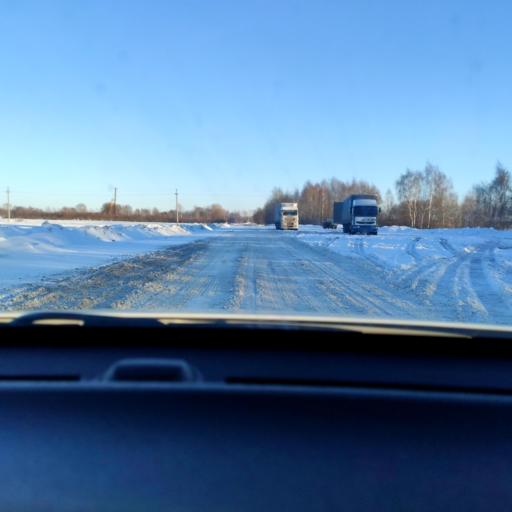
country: RU
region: Tatarstan
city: Stolbishchi
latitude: 55.6441
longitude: 49.2835
